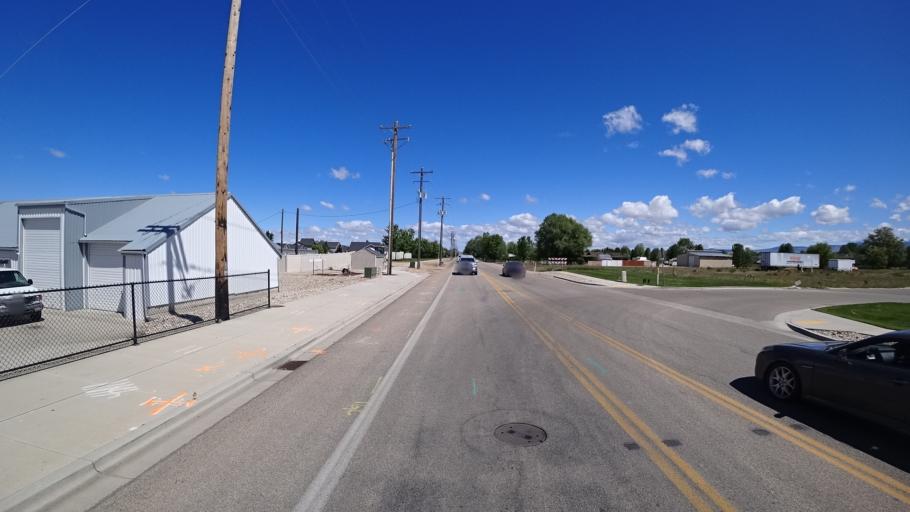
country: US
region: Idaho
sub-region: Ada County
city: Meridian
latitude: 43.6494
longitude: -116.3746
